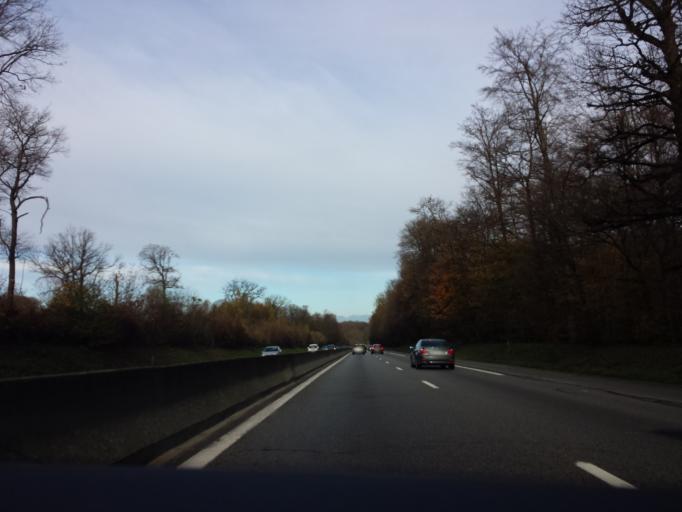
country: FR
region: Ile-de-France
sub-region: Departement des Yvelines
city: Saint-Nom-la-Breteche
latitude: 48.8873
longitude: 2.0117
